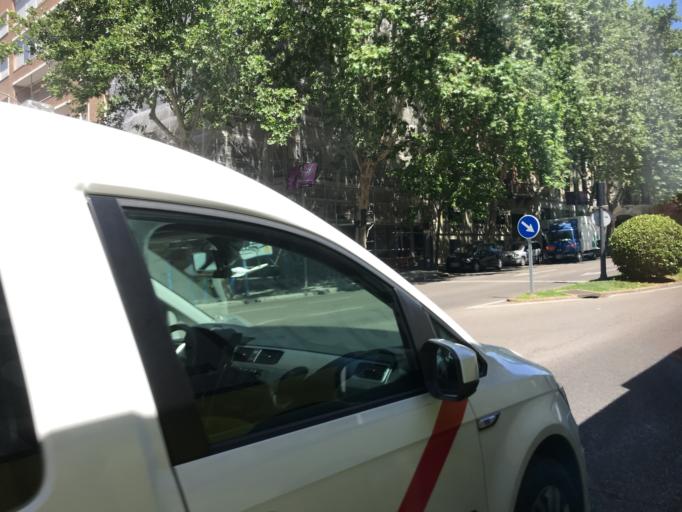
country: ES
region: Madrid
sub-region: Provincia de Madrid
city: Retiro
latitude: 40.4125
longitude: -3.6888
